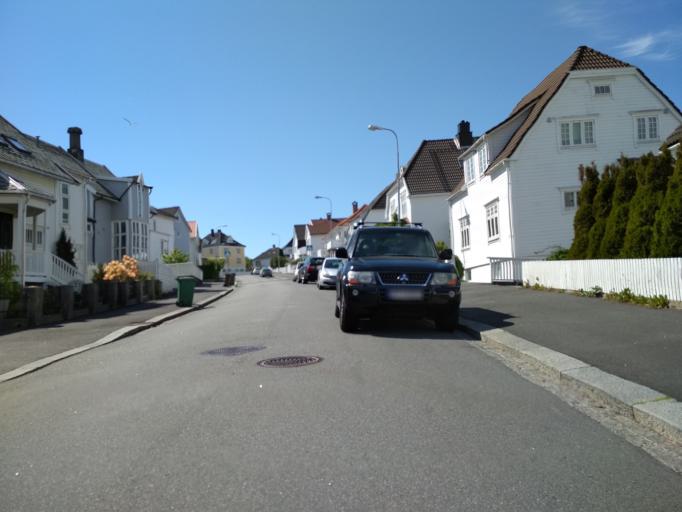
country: NO
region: Rogaland
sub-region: Stavanger
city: Stavanger
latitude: 58.9590
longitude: 5.7331
